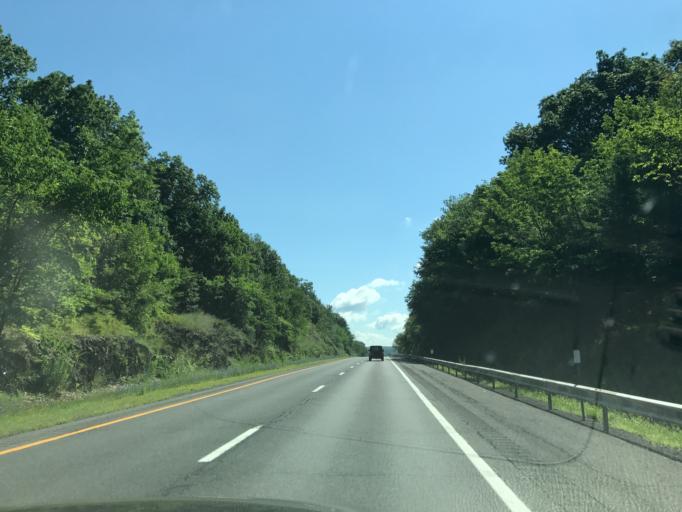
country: US
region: New York
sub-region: Columbia County
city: Niverville
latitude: 42.4823
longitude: -73.6595
